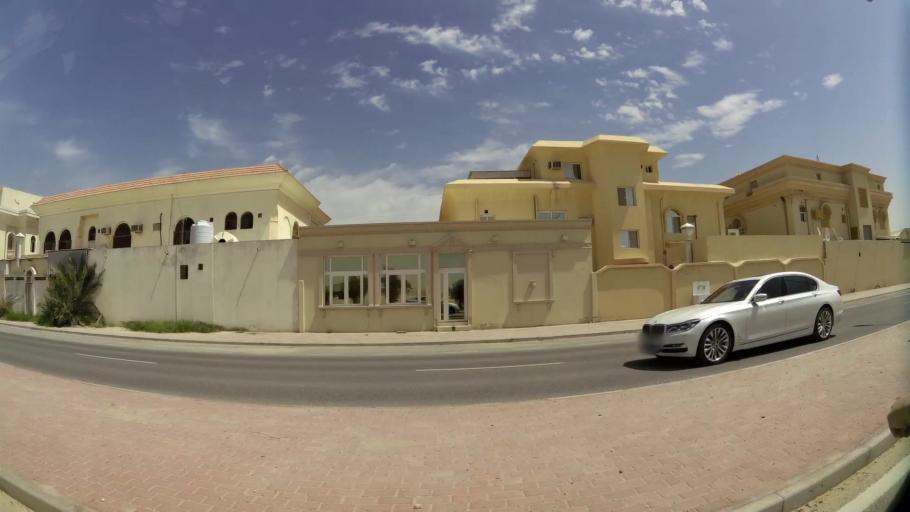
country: QA
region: Baladiyat ar Rayyan
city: Ar Rayyan
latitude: 25.2872
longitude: 51.4066
